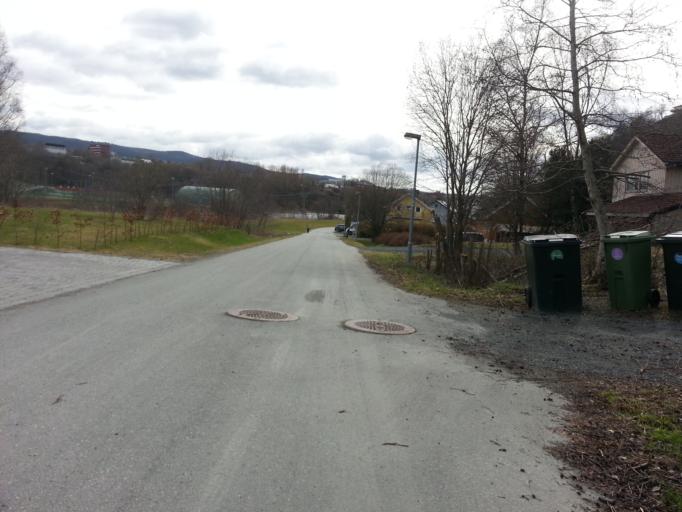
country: NO
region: Sor-Trondelag
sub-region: Trondheim
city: Trondheim
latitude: 63.4069
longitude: 10.3860
